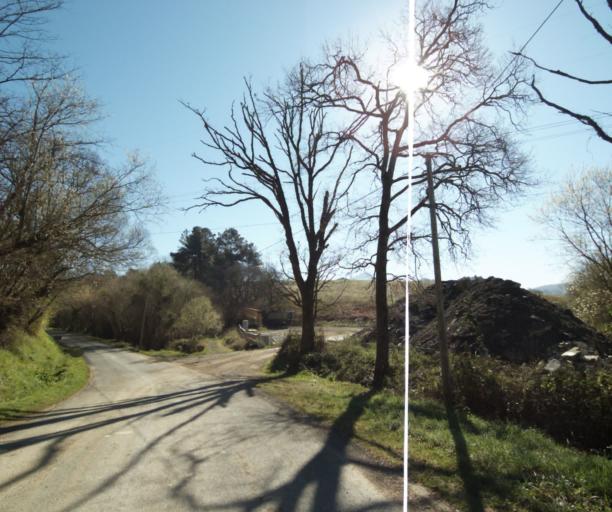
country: FR
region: Aquitaine
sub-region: Departement des Pyrenees-Atlantiques
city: Urrugne
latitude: 43.3459
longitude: -1.6869
